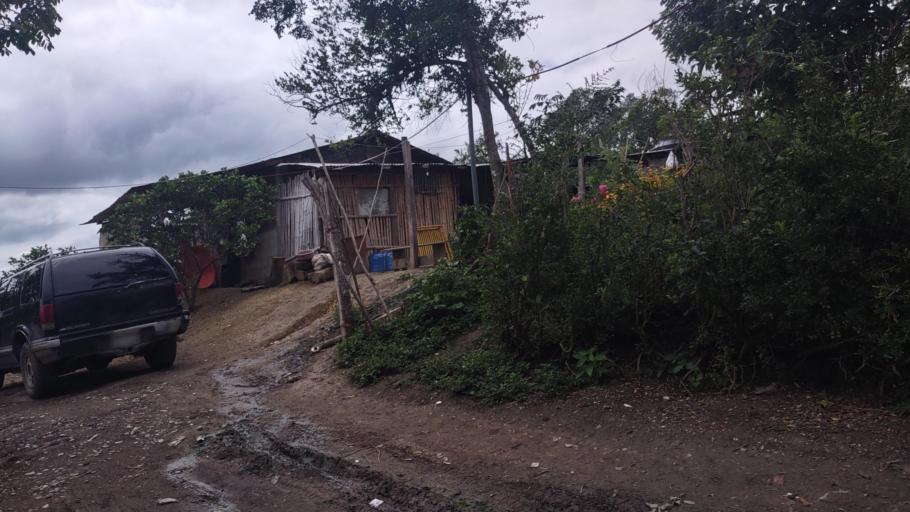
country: MX
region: Veracruz
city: Papantla de Olarte
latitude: 20.4671
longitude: -97.2741
